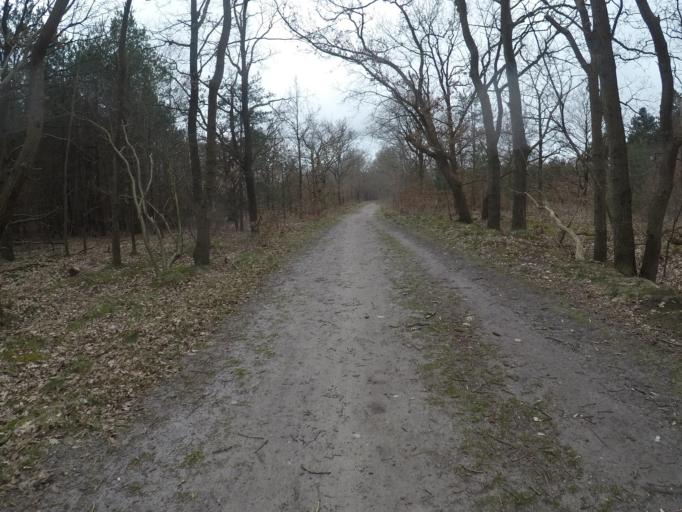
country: DE
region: Lower Saxony
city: Cuxhaven
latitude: 53.8391
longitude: 8.6349
